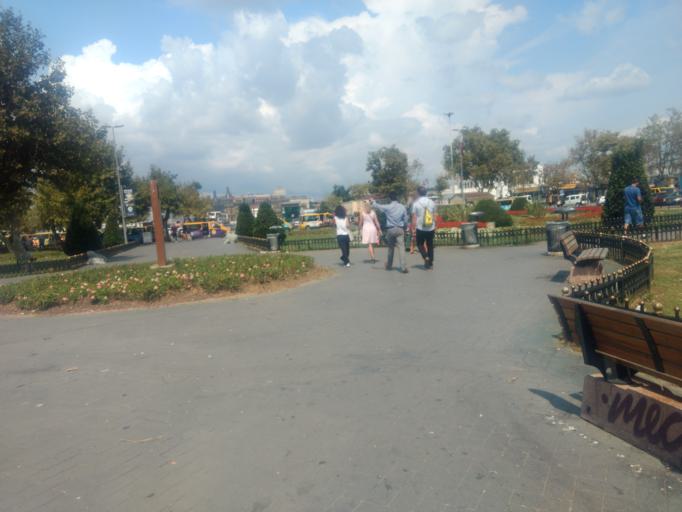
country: TR
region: Istanbul
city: UEskuedar
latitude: 40.9902
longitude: 29.0214
